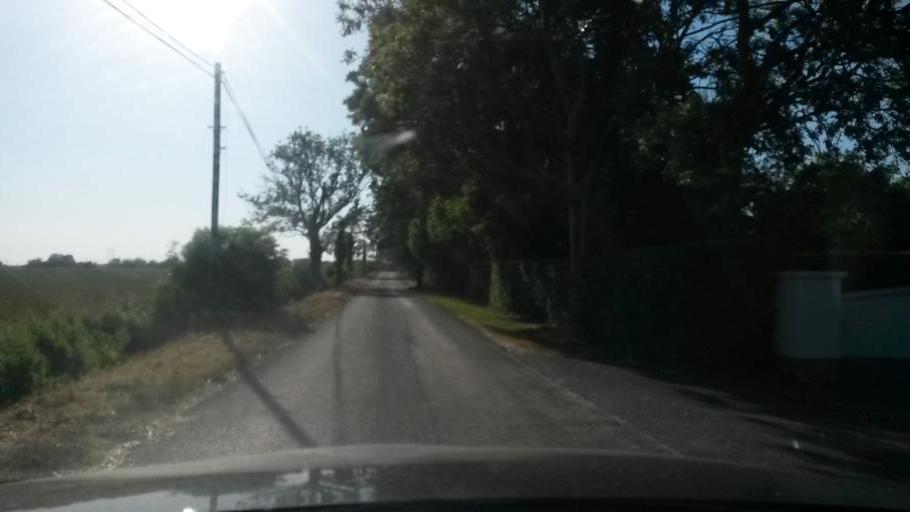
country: IE
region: Leinster
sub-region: Dublin City
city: Finglas
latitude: 53.4311
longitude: -6.3210
